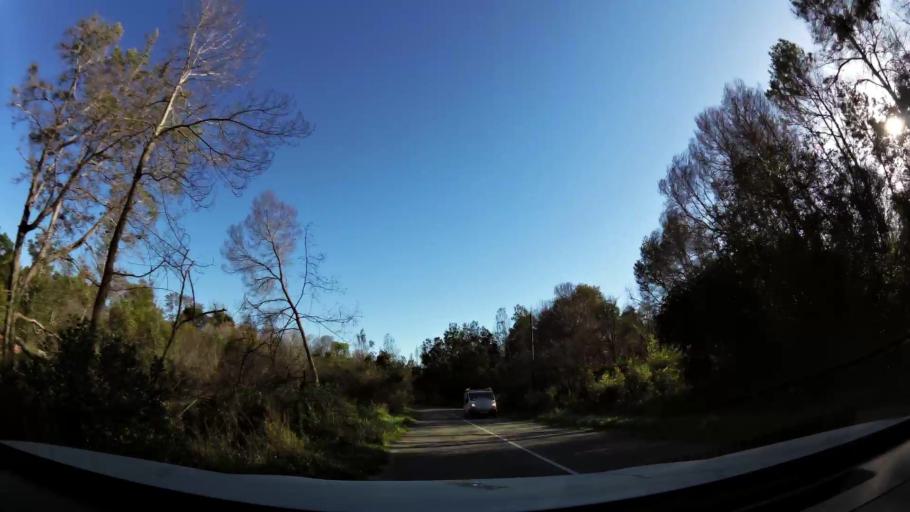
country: ZA
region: Western Cape
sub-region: Eden District Municipality
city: Knysna
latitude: -34.0316
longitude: 23.0147
